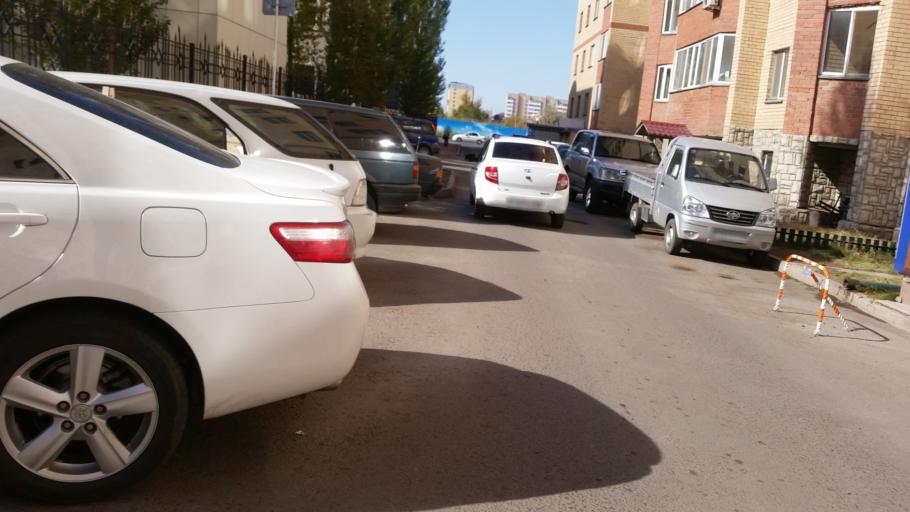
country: KZ
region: Astana Qalasy
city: Astana
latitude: 51.1551
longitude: 71.5049
